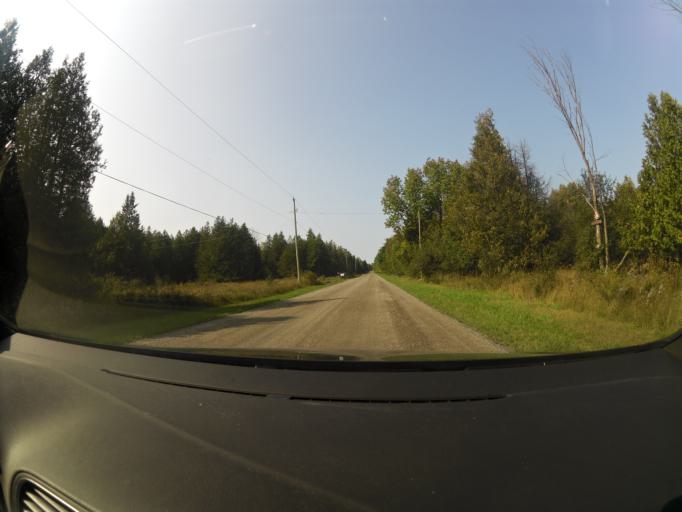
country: CA
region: Ontario
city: Carleton Place
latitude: 45.3231
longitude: -76.1485
